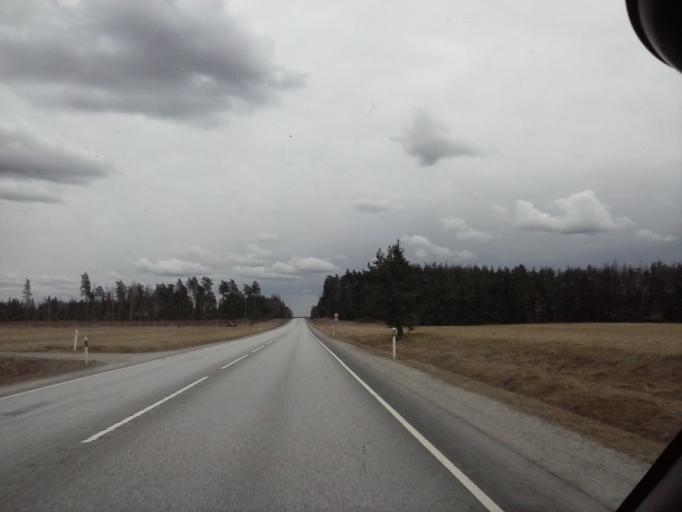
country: EE
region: Harju
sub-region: Anija vald
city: Kehra
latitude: 59.0927
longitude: 25.3905
